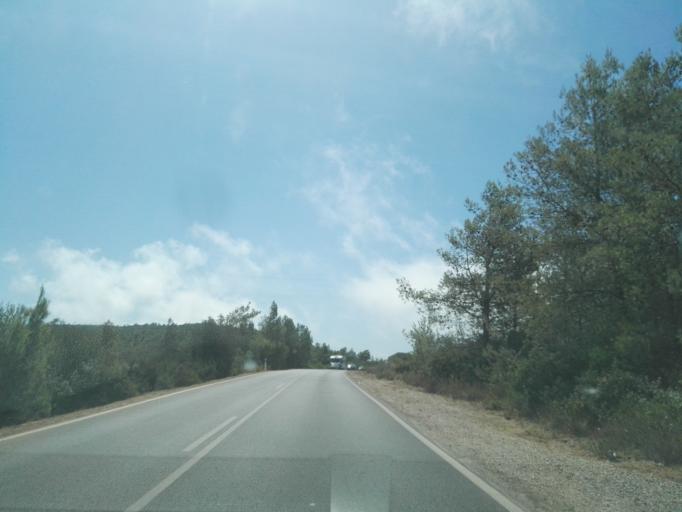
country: PT
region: Setubal
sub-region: Sesimbra
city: Sesimbra
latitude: 38.4519
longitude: -9.0898
